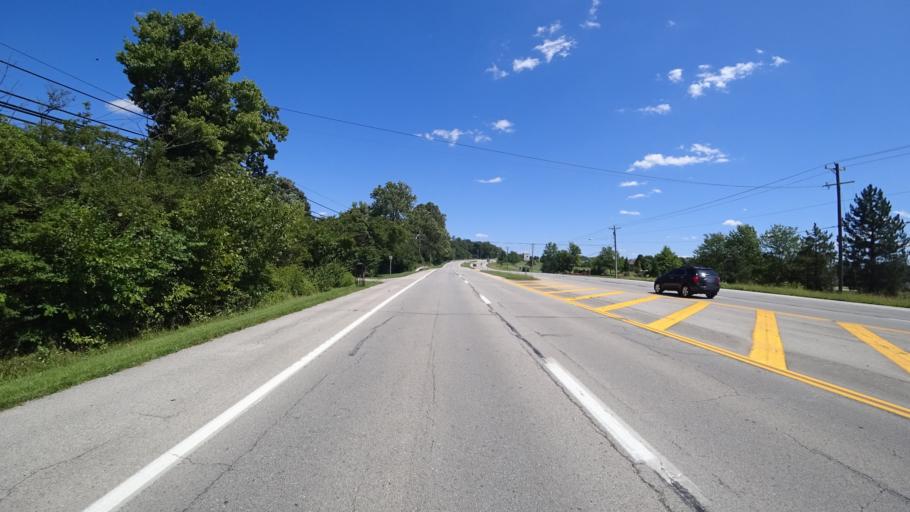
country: US
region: Ohio
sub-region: Butler County
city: New Miami
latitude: 39.4064
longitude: -84.5181
